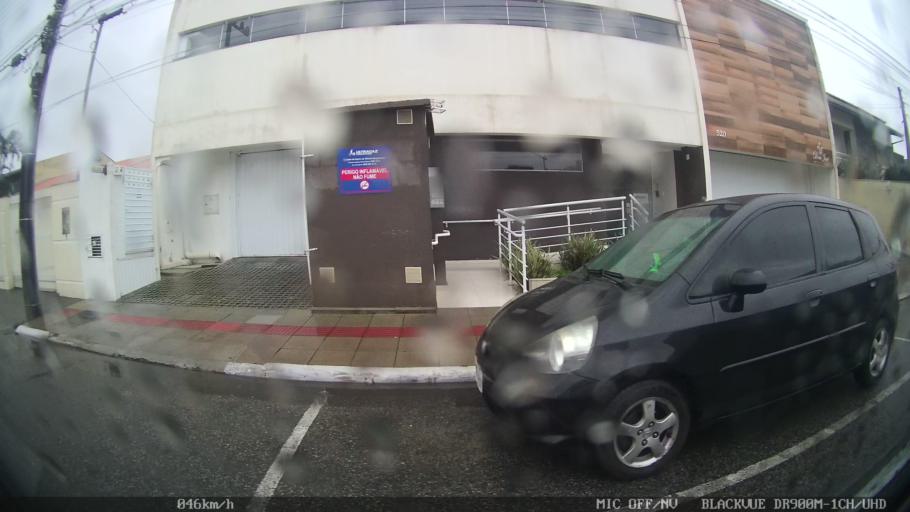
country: BR
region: Santa Catarina
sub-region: Itajai
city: Itajai
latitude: -26.9000
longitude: -48.6767
